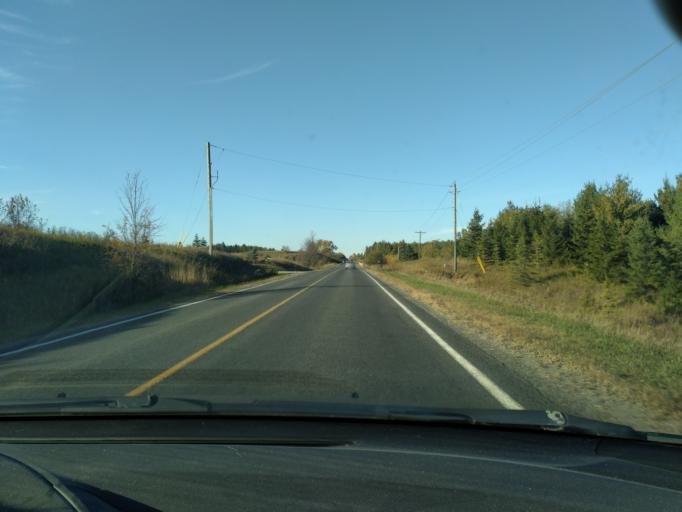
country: CA
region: Ontario
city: Bradford West Gwillimbury
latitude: 43.9401
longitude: -79.7128
